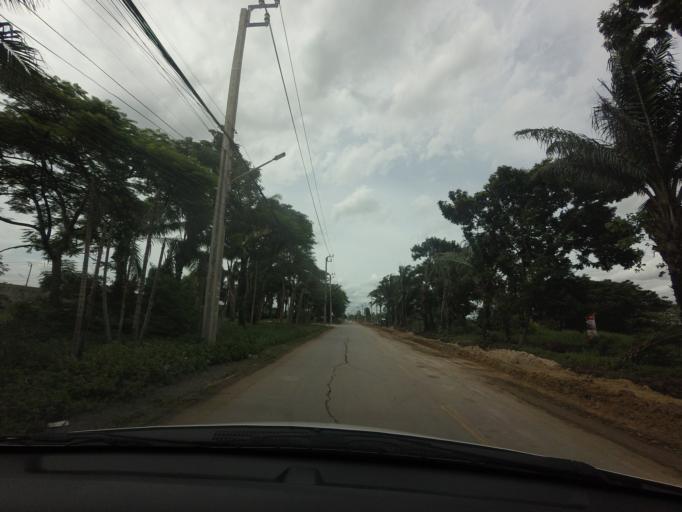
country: TH
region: Bangkok
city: Min Buri
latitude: 13.7814
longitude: 100.7613
